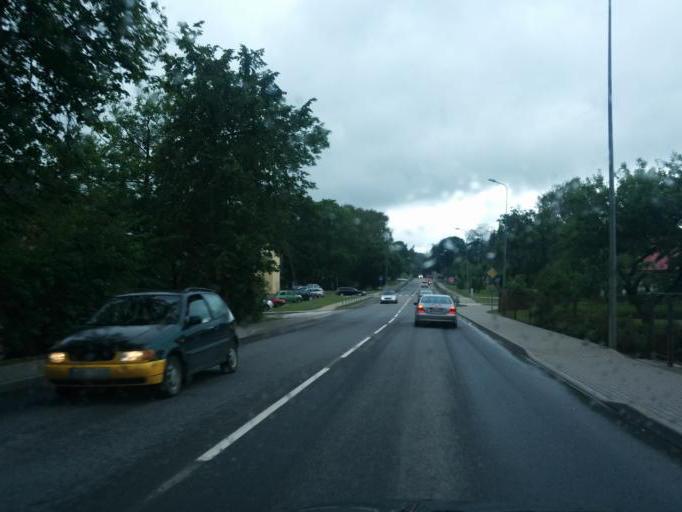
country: LV
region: Smiltene
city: Smiltene
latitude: 57.4207
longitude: 25.9073
